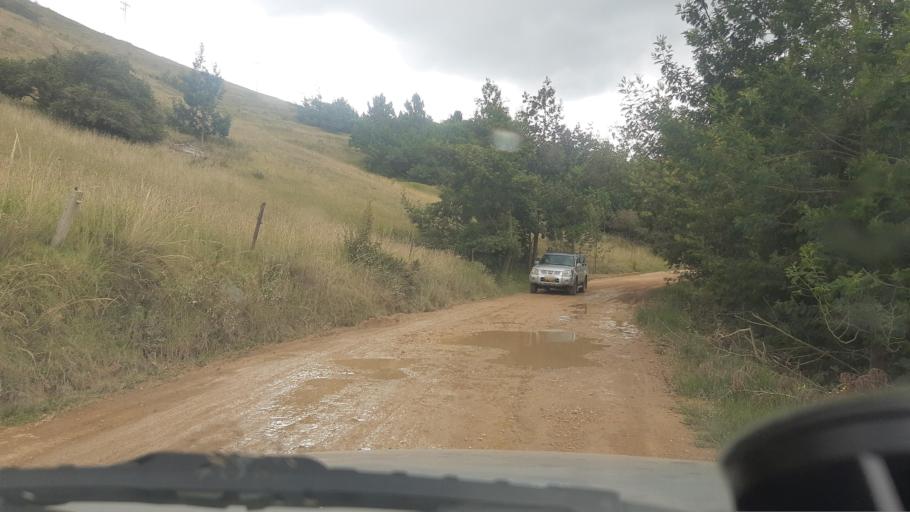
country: CO
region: Cundinamarca
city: Suesca
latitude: 5.1640
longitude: -73.8013
